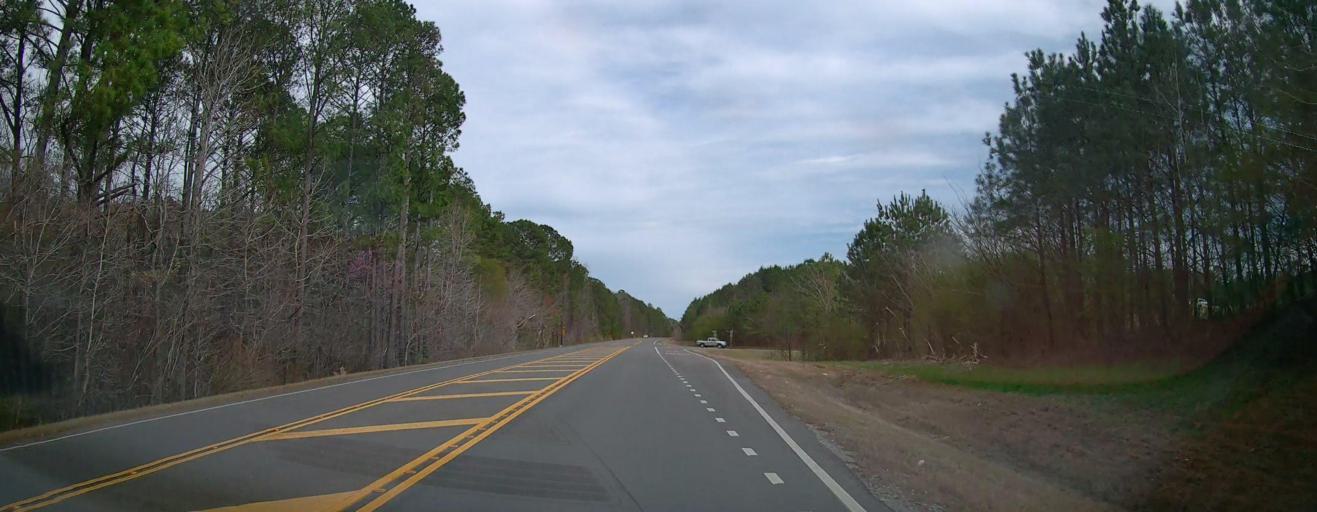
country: US
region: Alabama
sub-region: Walker County
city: Jasper
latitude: 33.8635
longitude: -87.3943
